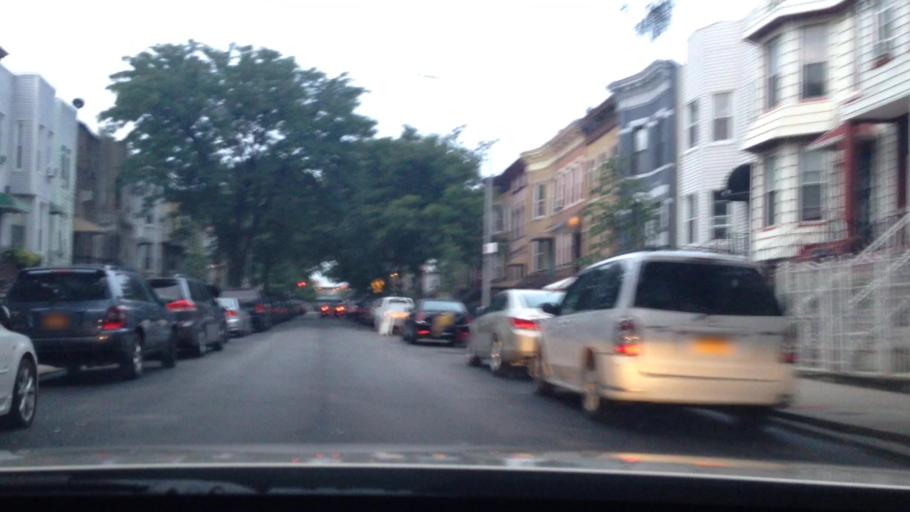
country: US
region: New York
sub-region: Kings County
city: East New York
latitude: 40.6859
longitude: -73.9080
